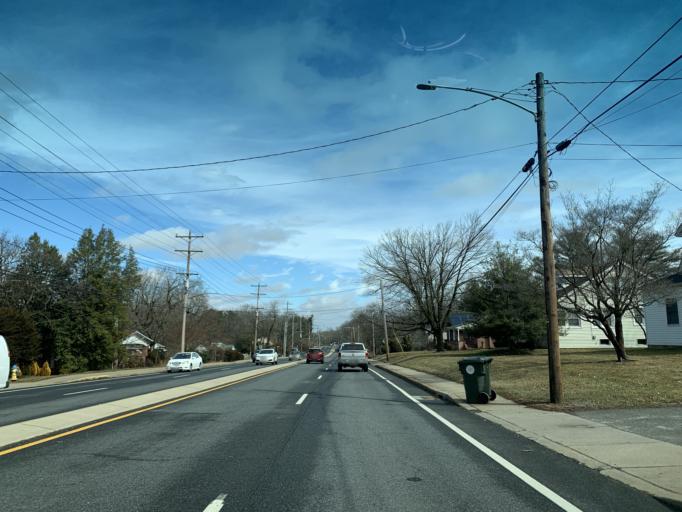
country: US
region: Delaware
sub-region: New Castle County
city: Newark
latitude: 39.6899
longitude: -75.7313
